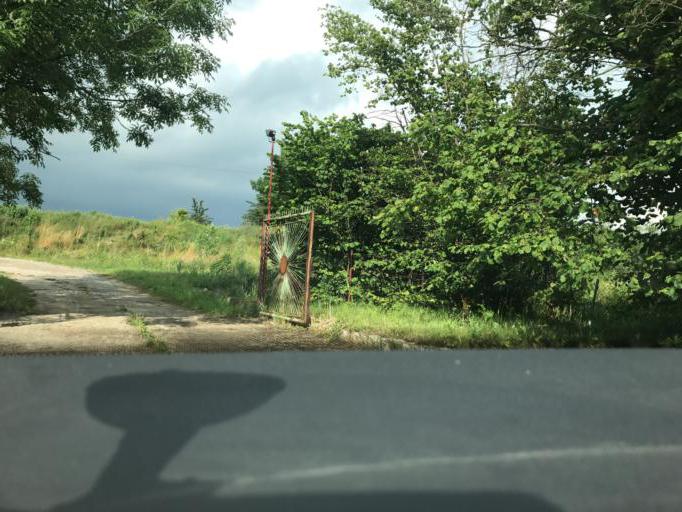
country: PL
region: Pomeranian Voivodeship
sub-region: Powiat gdanski
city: Cedry Wielkie
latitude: 54.3371
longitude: 18.8042
